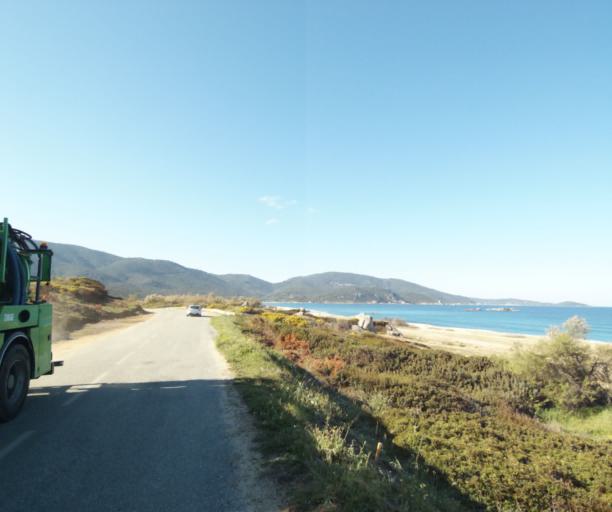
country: FR
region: Corsica
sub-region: Departement de la Corse-du-Sud
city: Propriano
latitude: 41.6667
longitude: 8.8825
